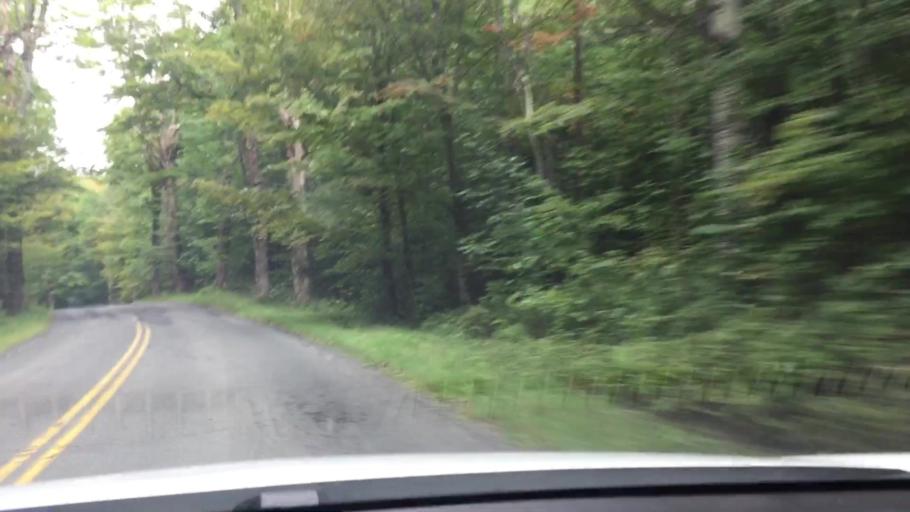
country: US
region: Massachusetts
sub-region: Berkshire County
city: Becket
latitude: 42.3009
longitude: -73.1351
